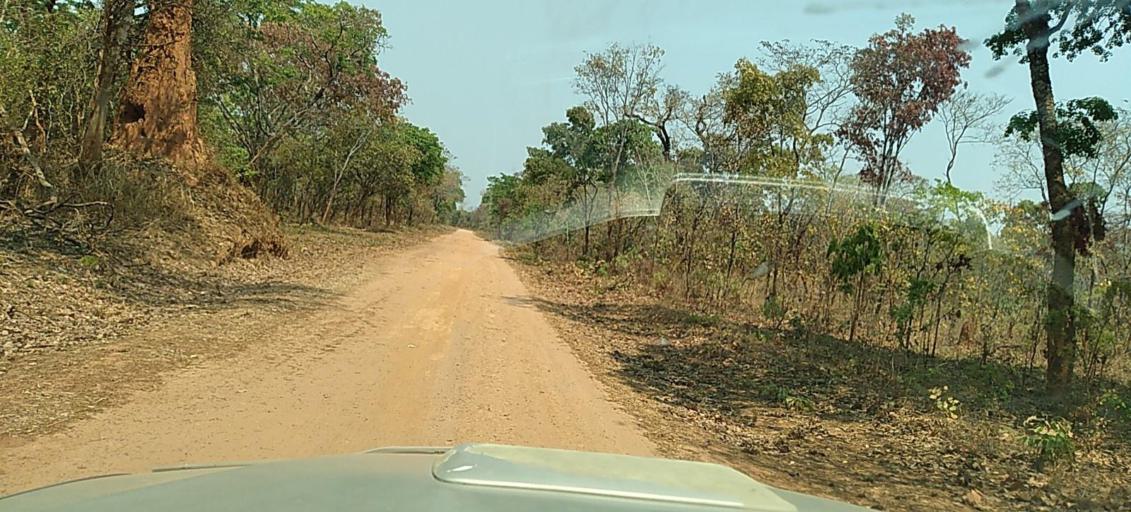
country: ZM
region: North-Western
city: Kasempa
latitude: -13.6880
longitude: 26.3212
